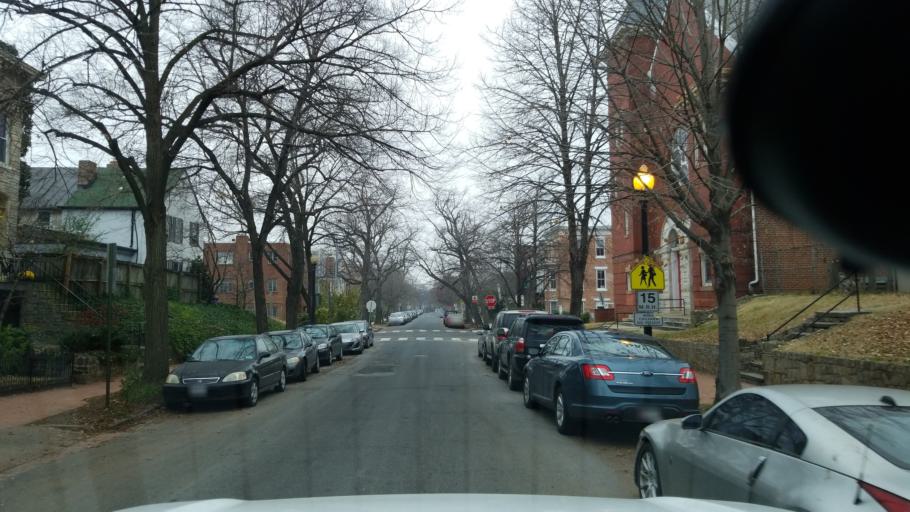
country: US
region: Washington, D.C.
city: Washington, D.C.
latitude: 38.8843
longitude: -76.9999
